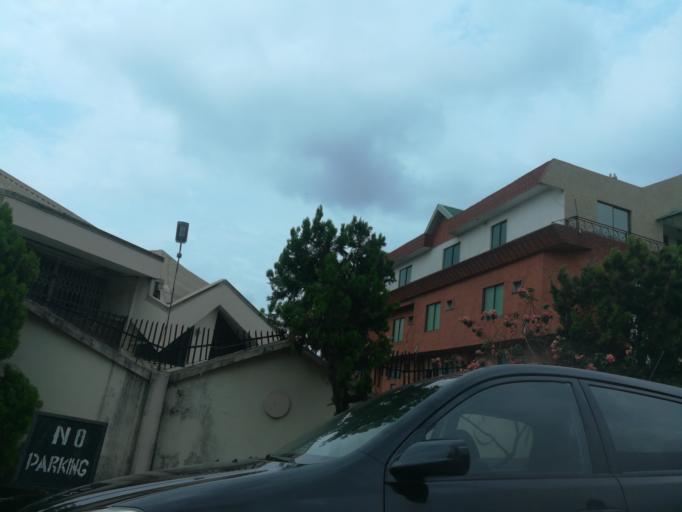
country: NG
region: Lagos
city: Ojota
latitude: 6.5835
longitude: 3.3661
